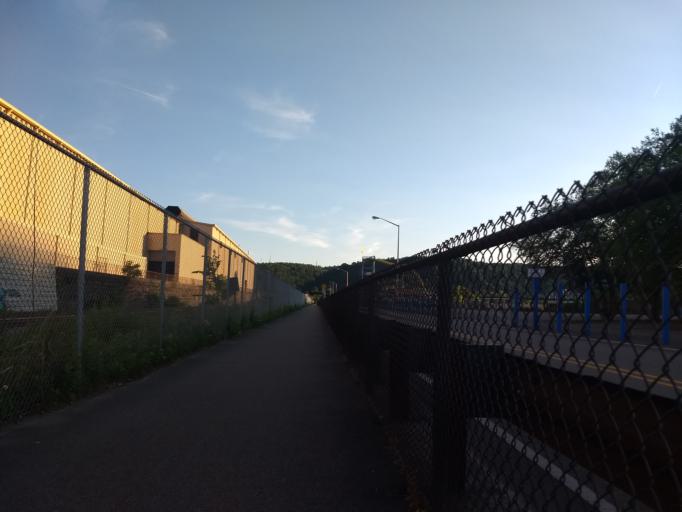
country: US
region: Pennsylvania
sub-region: Allegheny County
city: West Homestead
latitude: 40.3998
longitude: -79.9239
